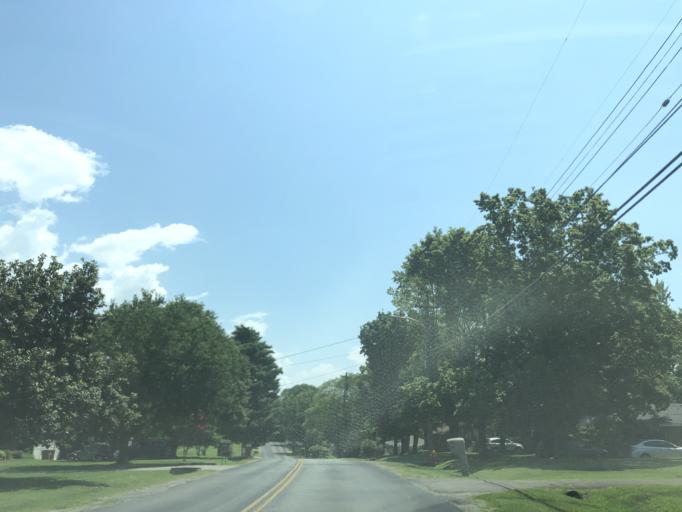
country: US
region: Tennessee
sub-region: Davidson County
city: Lakewood
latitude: 36.1543
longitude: -86.6616
